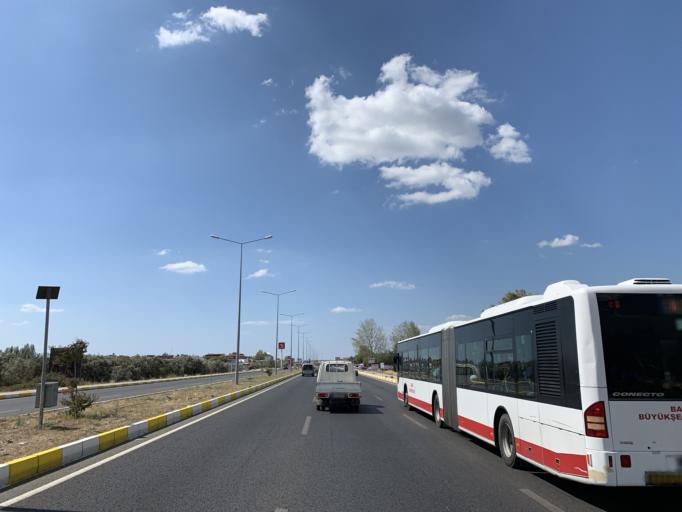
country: TR
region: Balikesir
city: Edremit
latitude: 39.5943
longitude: 26.9397
